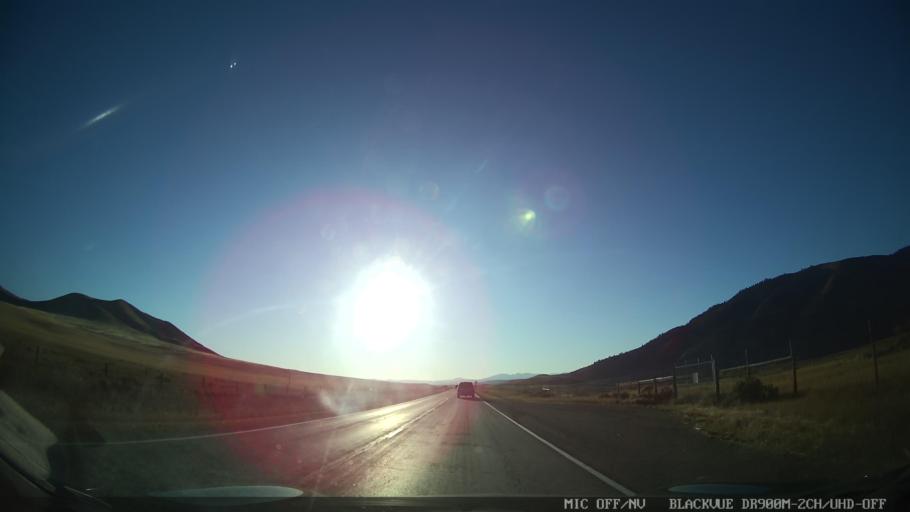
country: US
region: Colorado
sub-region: Grand County
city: Kremmling
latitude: 40.0525
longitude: -106.3575
